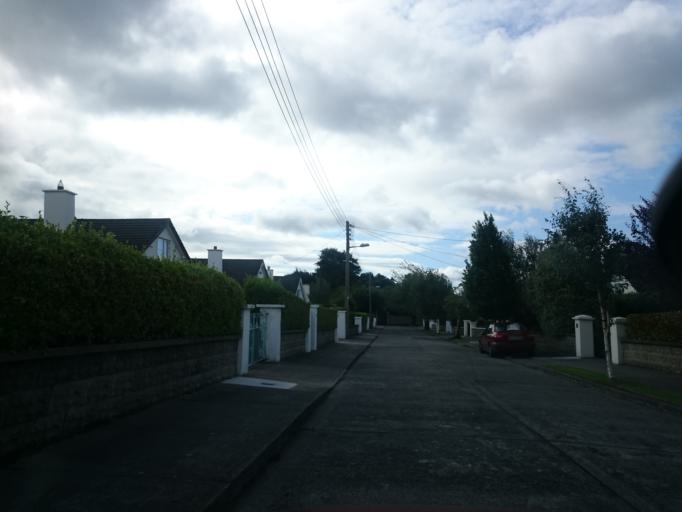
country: IE
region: Leinster
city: Mount Merrion
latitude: 53.2910
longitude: -6.2064
